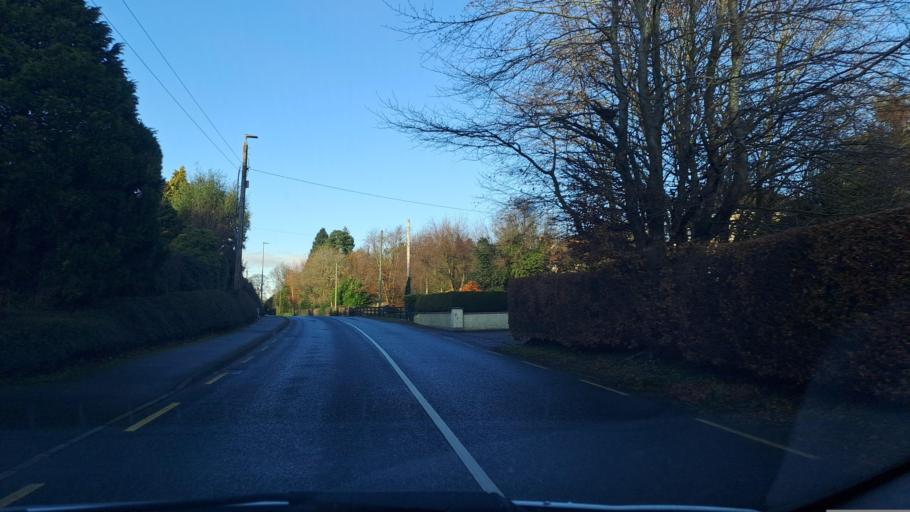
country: IE
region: Ulster
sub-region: An Cabhan
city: Bailieborough
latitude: 53.9099
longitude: -6.9684
